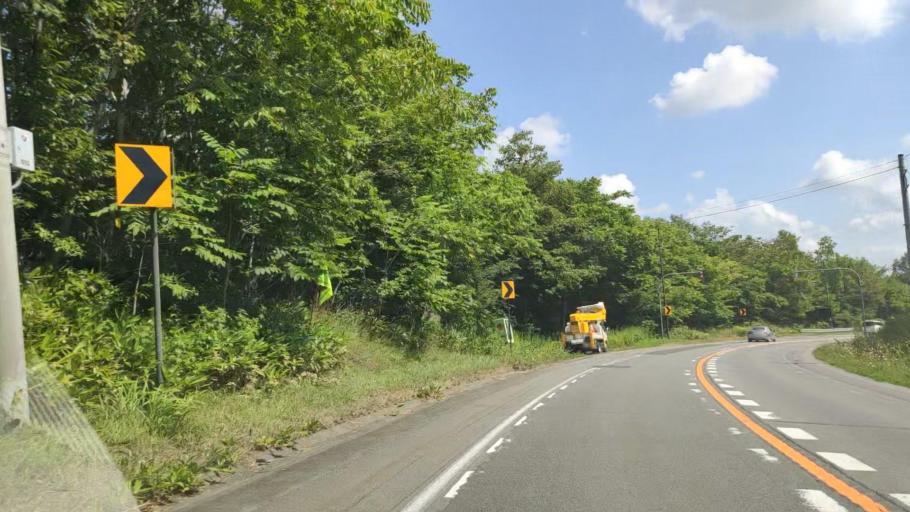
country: JP
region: Hokkaido
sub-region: Asahikawa-shi
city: Asahikawa
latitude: 43.5834
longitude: 142.4375
